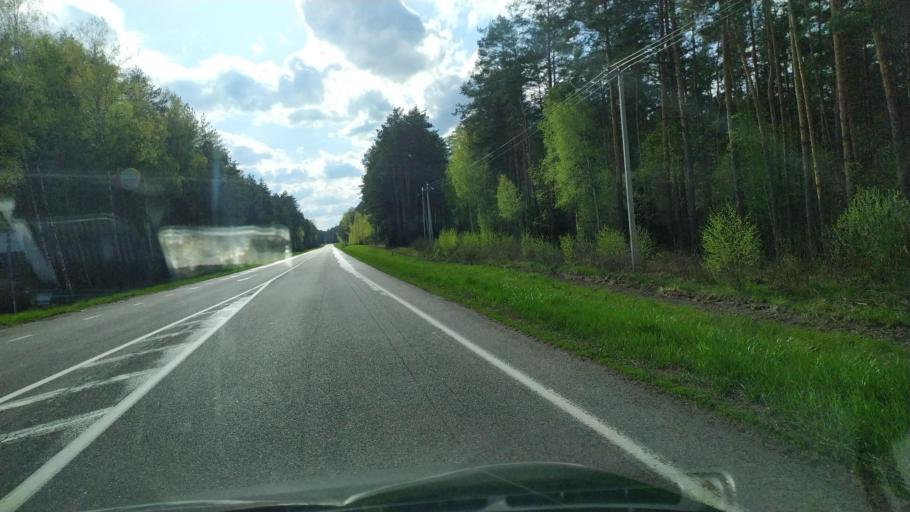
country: BY
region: Brest
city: Pruzhany
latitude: 52.7022
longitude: 24.3032
